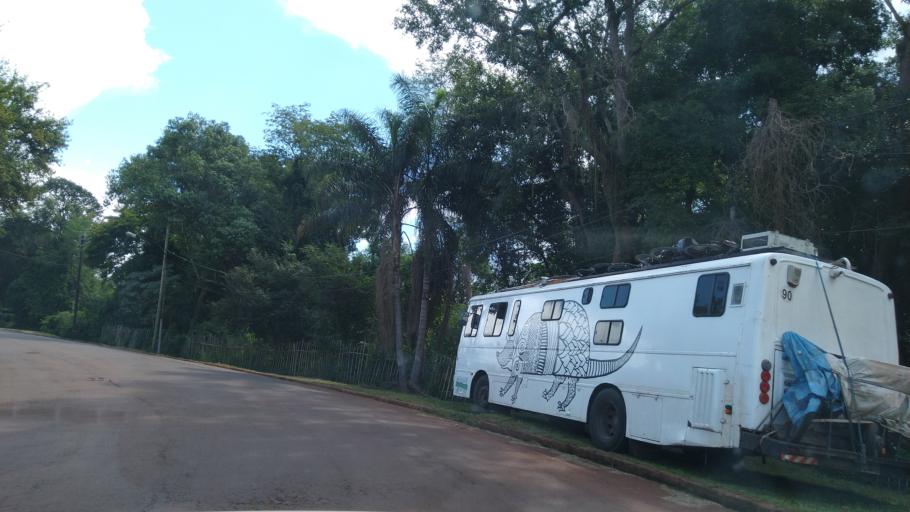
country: AR
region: Misiones
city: Puerto Libertad
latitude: -25.9679
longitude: -54.5835
